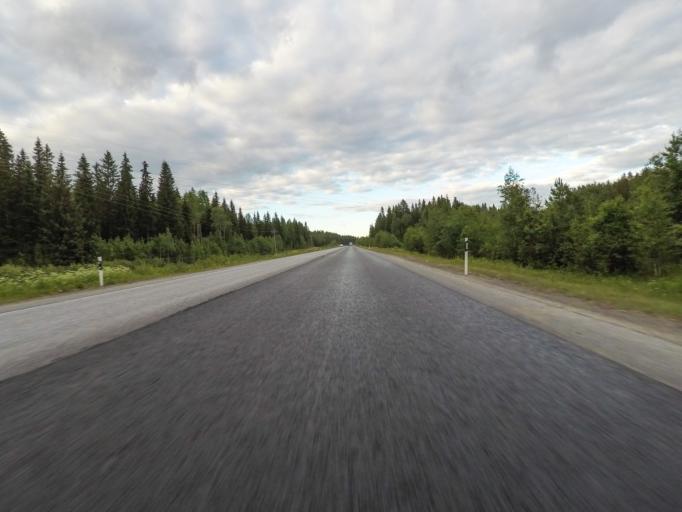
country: FI
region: Southern Savonia
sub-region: Mikkeli
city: Pertunmaa
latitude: 61.4322
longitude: 26.4738
